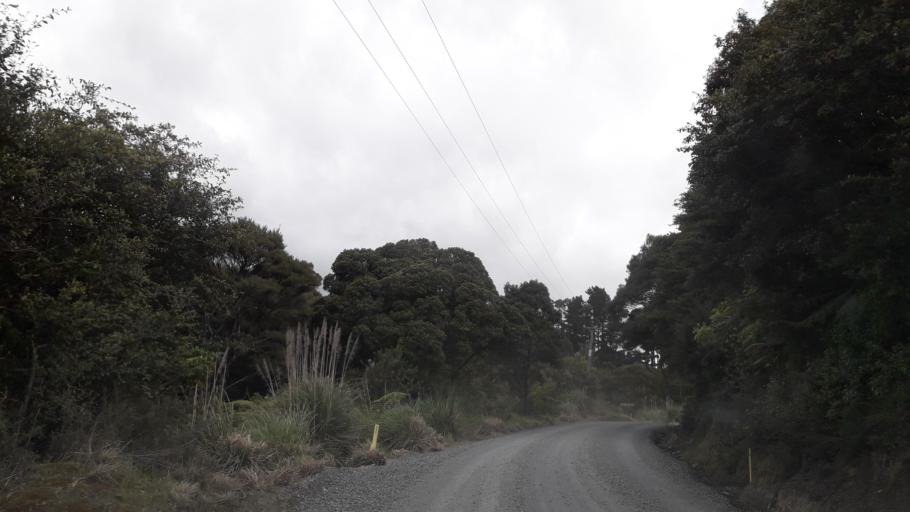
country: NZ
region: Northland
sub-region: Far North District
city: Kerikeri
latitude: -35.1164
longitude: 173.7532
